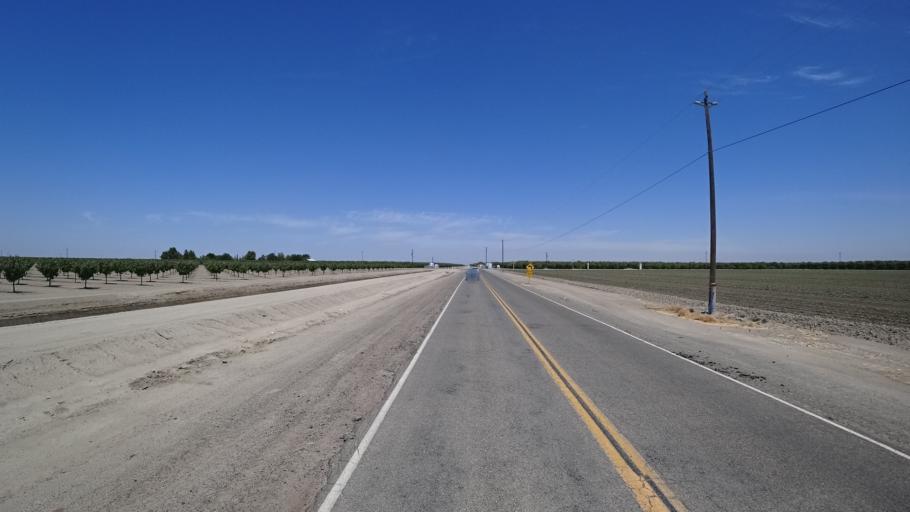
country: US
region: California
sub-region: Kings County
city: Corcoran
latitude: 36.1144
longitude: -119.6257
